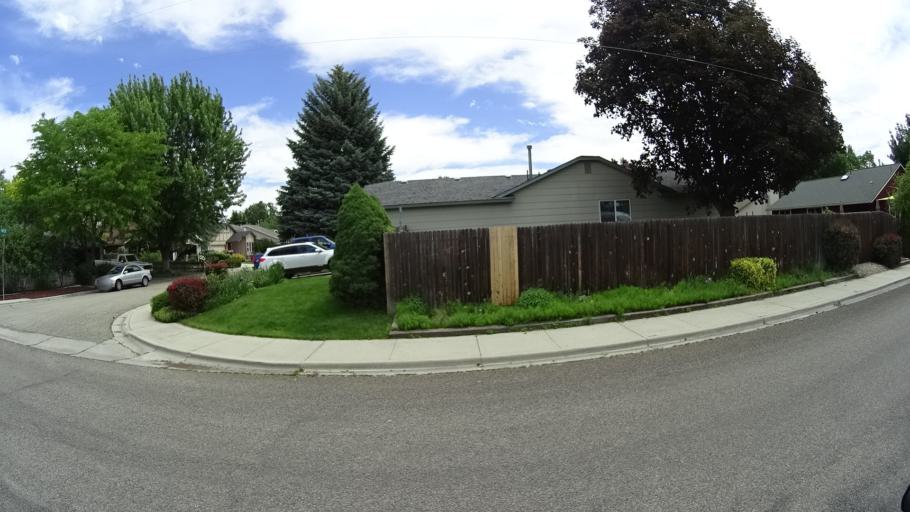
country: US
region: Idaho
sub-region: Ada County
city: Eagle
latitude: 43.6471
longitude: -116.3243
